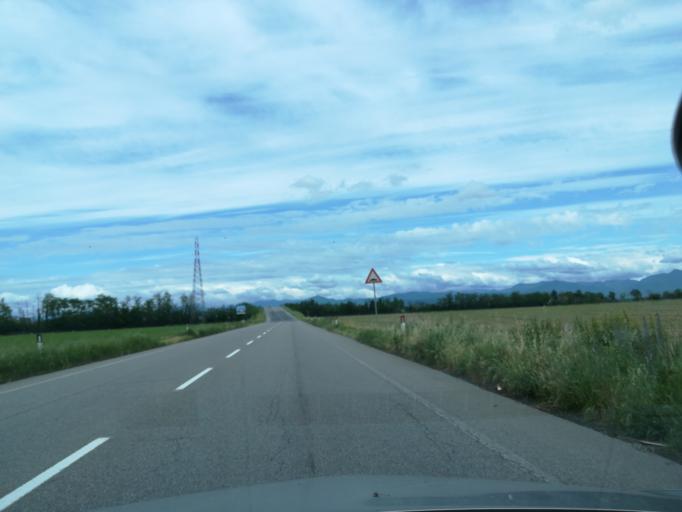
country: IT
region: Lombardy
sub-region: Provincia di Bergamo
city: Calcio
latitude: 45.5288
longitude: 9.8333
